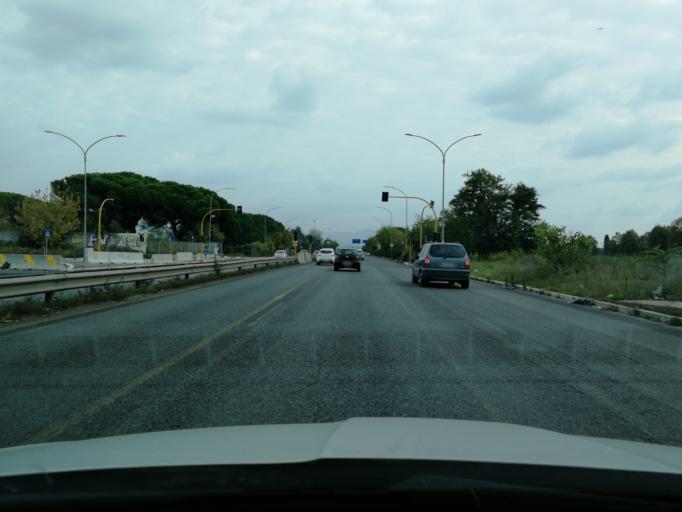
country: IT
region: Latium
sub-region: Citta metropolitana di Roma Capitale
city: Ciampino
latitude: 41.8465
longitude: 12.5785
